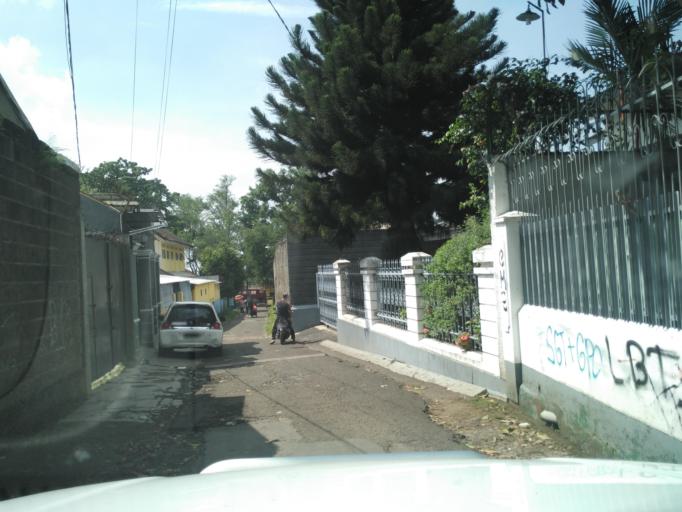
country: ID
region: West Java
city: Ciranjang-hilir
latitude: -6.8182
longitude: 107.1466
